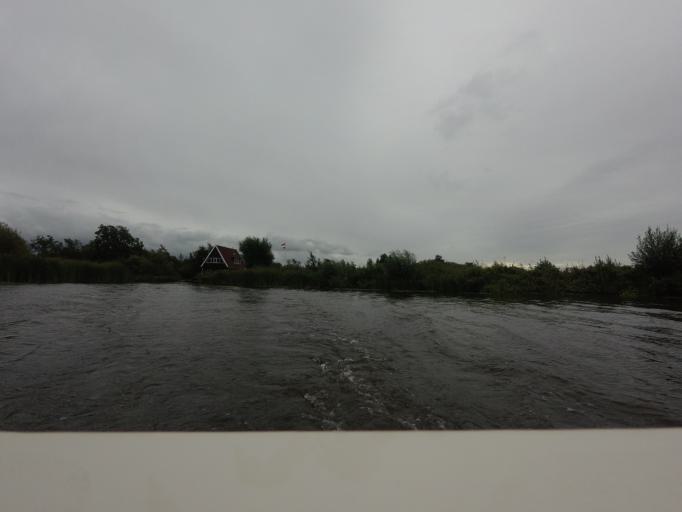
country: NL
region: Friesland
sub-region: Gemeente Boarnsterhim
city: Warten
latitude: 53.1242
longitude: 5.9278
